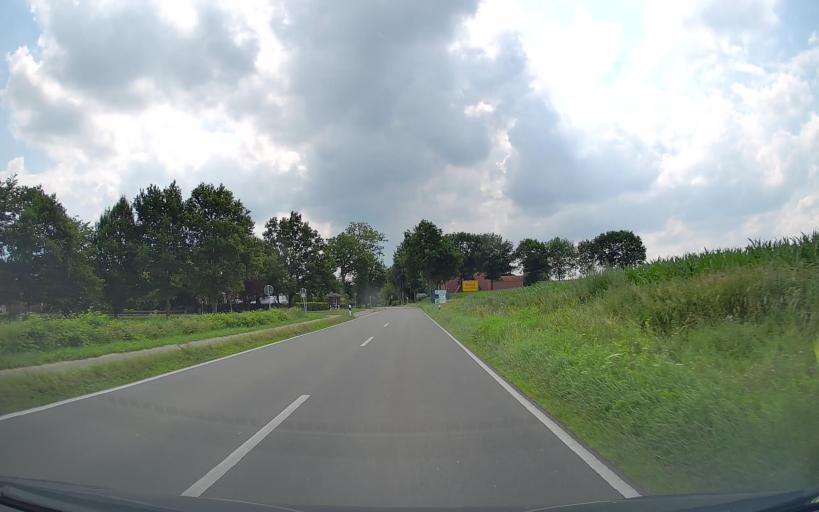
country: DE
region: Lower Saxony
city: Bosel
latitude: 53.0116
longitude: 7.9538
